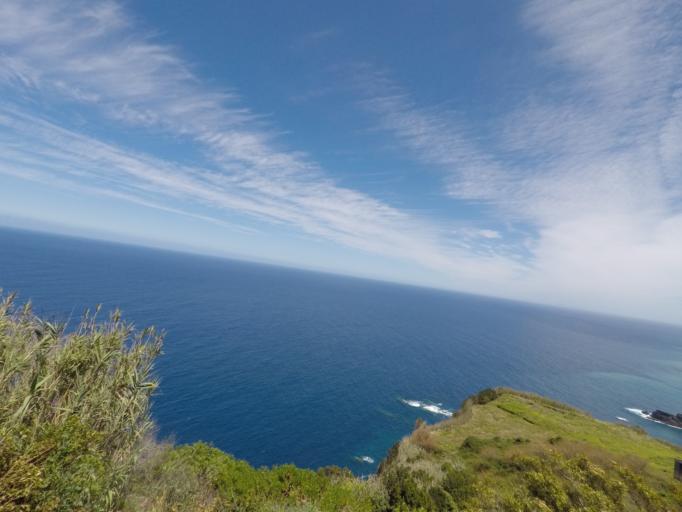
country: PT
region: Madeira
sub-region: Sao Vicente
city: Sao Vicente
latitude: 32.8261
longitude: -16.9795
